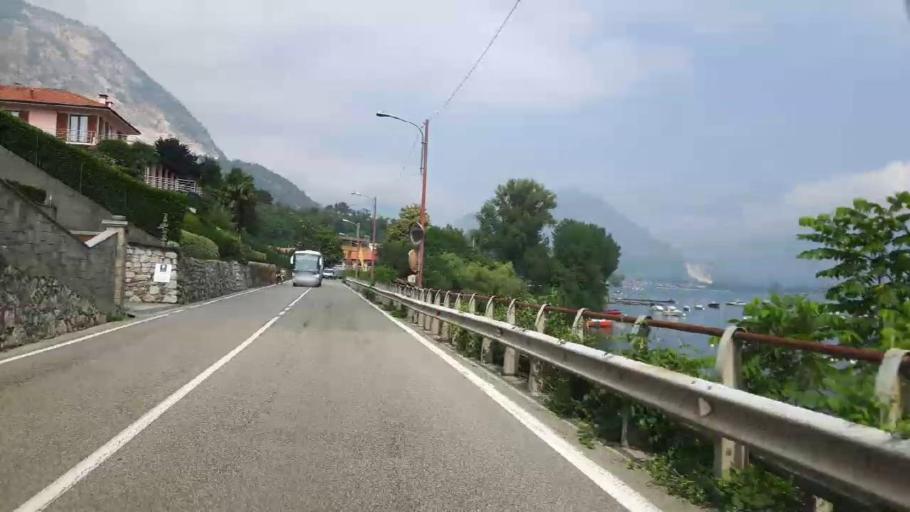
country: IT
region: Piedmont
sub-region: Provincia Verbano-Cusio-Ossola
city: Baveno
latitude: 45.9166
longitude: 8.5006
